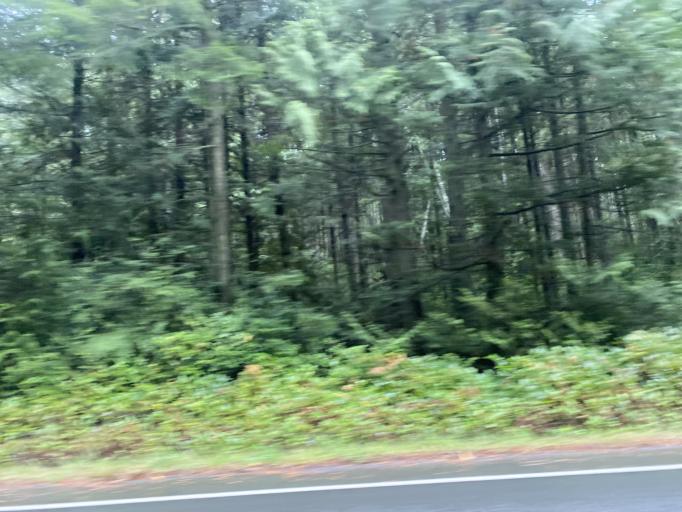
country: US
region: Washington
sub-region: Island County
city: Langley
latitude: 48.0497
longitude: -122.4501
